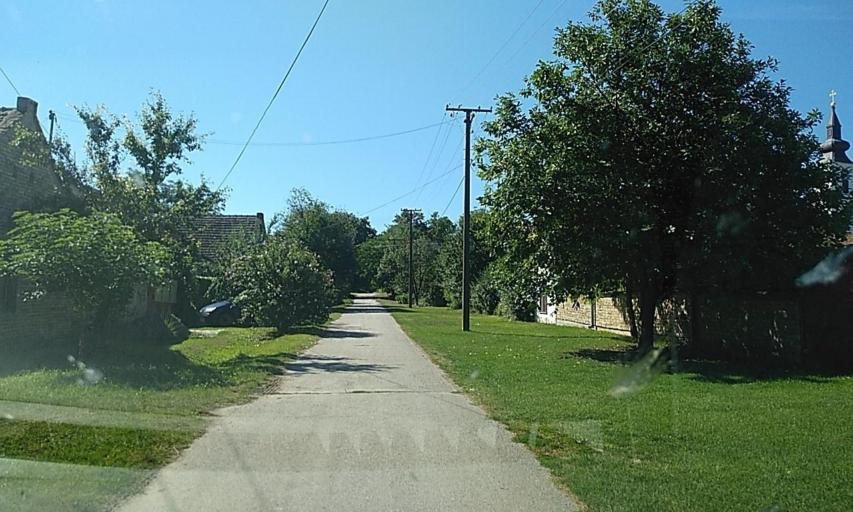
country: RS
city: Backo Gradiste
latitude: 45.5397
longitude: 20.0357
